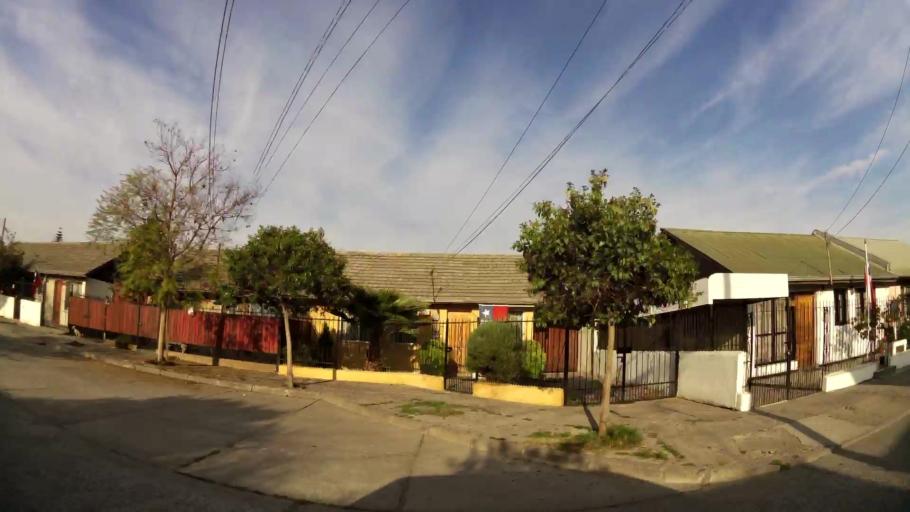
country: CL
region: Santiago Metropolitan
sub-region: Provincia de Maipo
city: San Bernardo
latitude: -33.5268
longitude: -70.6755
